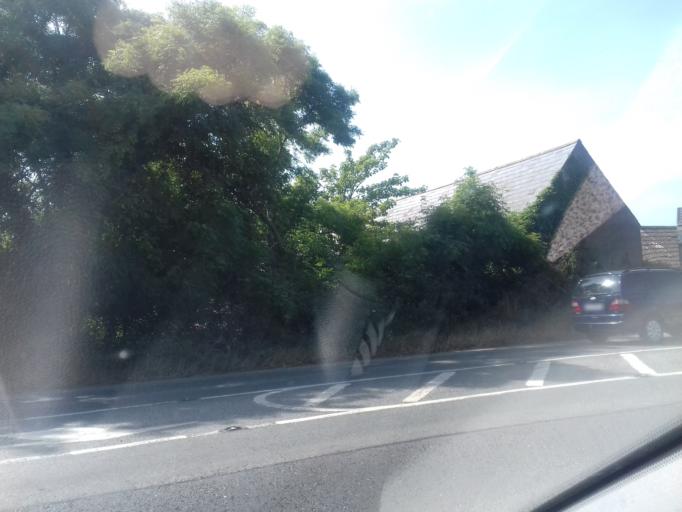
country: IE
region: Leinster
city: Lusk
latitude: 53.5185
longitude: -6.1907
